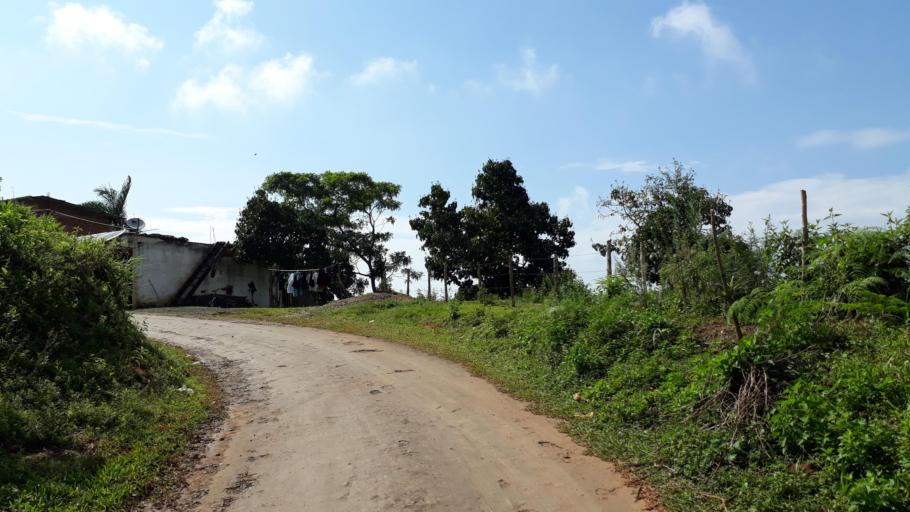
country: CO
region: Valle del Cauca
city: Jamundi
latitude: 3.2685
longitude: -76.6270
